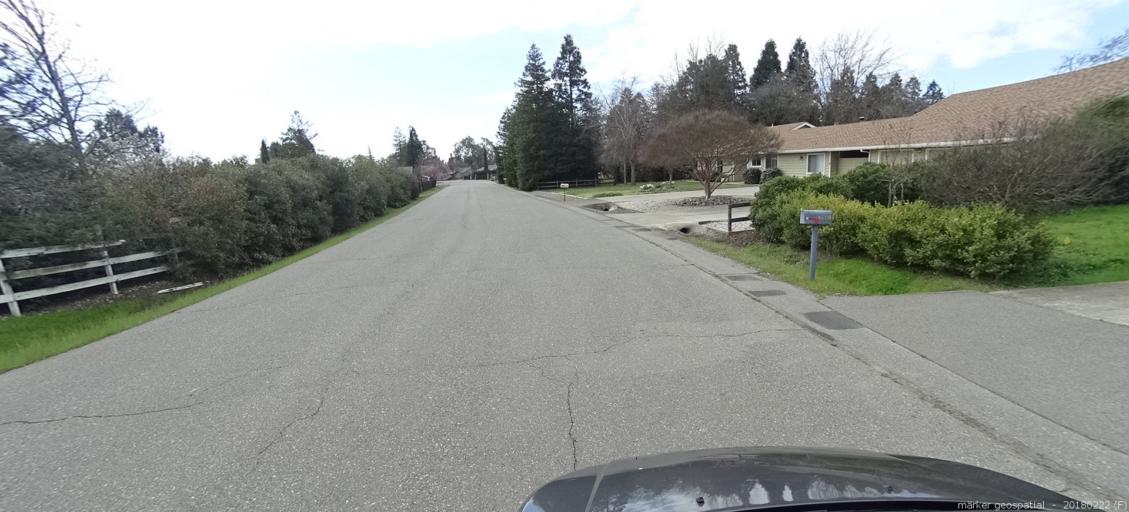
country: US
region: California
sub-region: Sacramento County
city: Rio Linda
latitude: 38.7132
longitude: -121.4193
